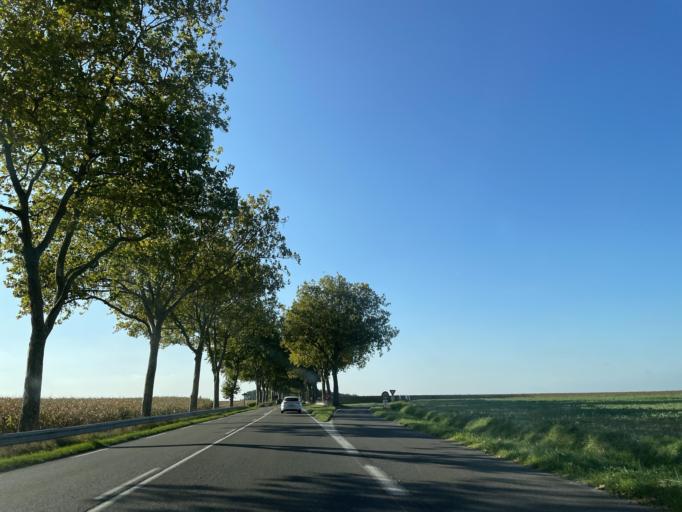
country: FR
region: Ile-de-France
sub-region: Departement de Seine-et-Marne
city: Guerard
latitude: 48.8392
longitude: 2.9693
